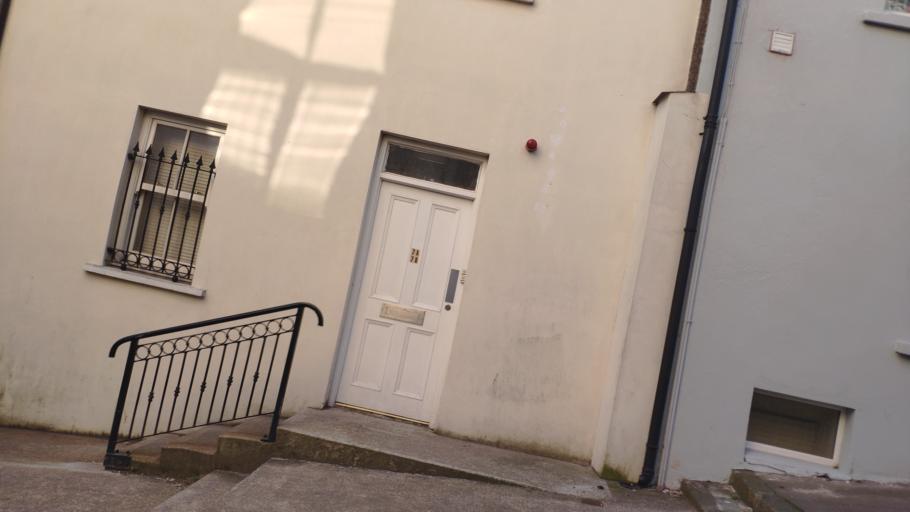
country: IE
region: Munster
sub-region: County Cork
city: Cork
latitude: 51.9030
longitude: -8.4711
